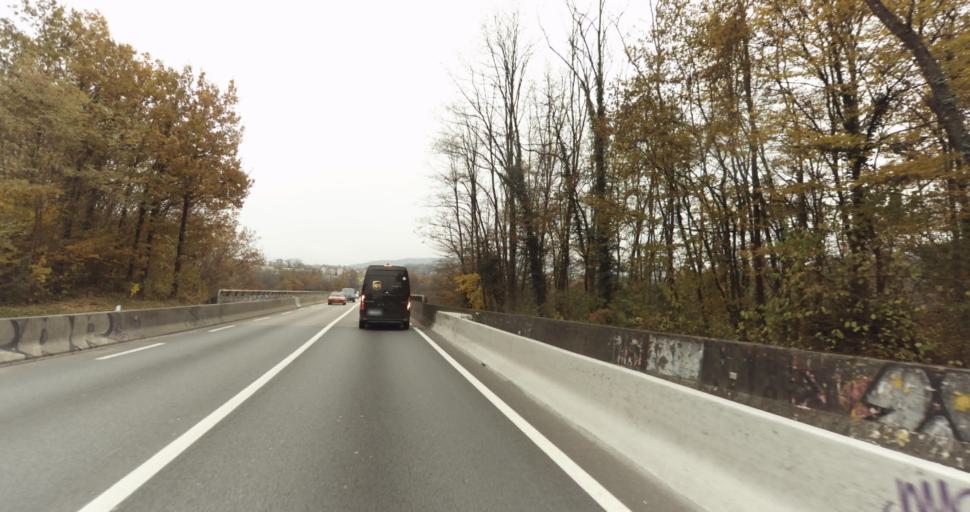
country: FR
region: Rhone-Alpes
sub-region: Departement de la Haute-Savoie
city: Meythet
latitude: 45.9089
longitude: 6.0851
